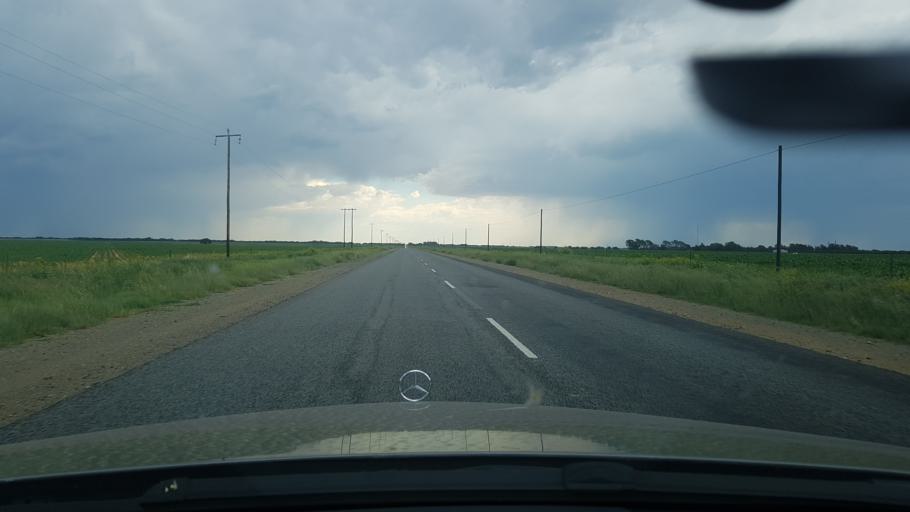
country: ZA
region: Orange Free State
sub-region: Lejweleputswa District Municipality
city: Hoopstad
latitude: -27.9669
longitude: 25.6852
